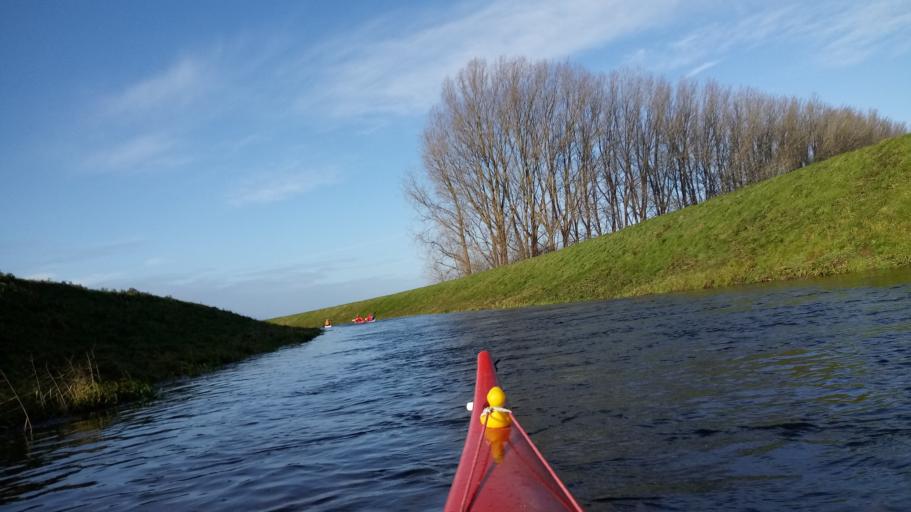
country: NL
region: Gelderland
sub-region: Gemeente Bronckhorst
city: Baak
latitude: 52.0995
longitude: 6.2254
